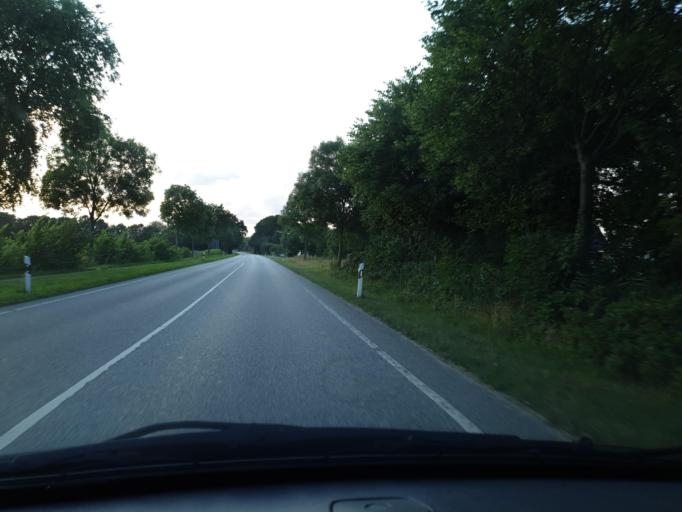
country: DE
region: Schleswig-Holstein
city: Schmedeswurth
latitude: 53.9191
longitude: 9.0478
